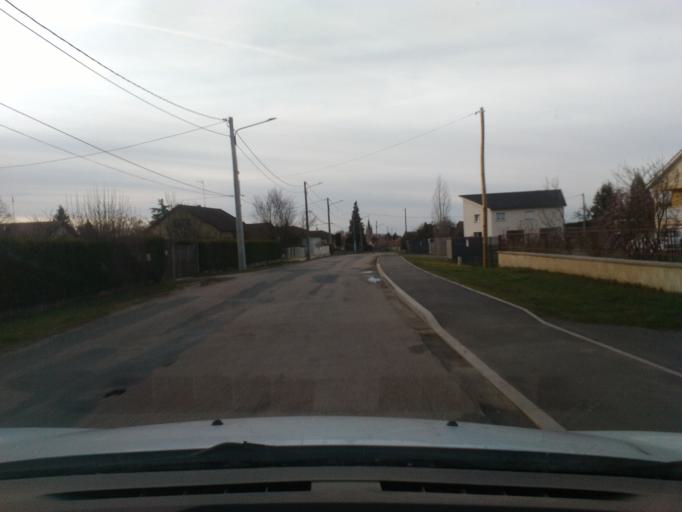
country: FR
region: Lorraine
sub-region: Departement des Vosges
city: Rambervillers
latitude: 48.3411
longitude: 6.6457
